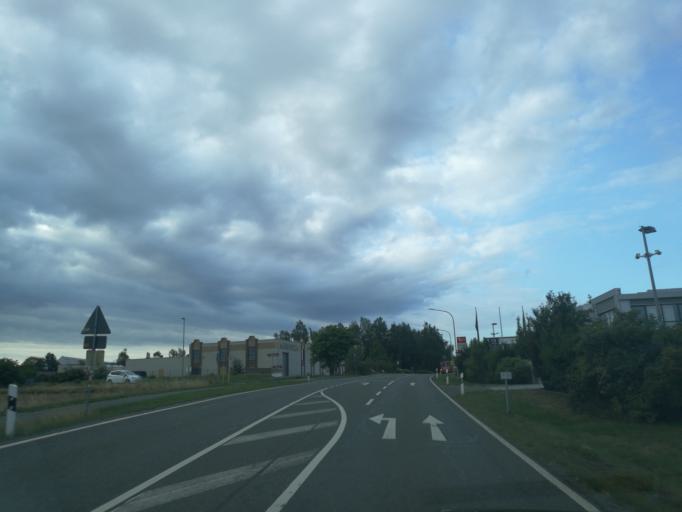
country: DE
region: Bavaria
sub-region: Upper Franconia
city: Dohlau
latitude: 50.2909
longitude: 11.9441
